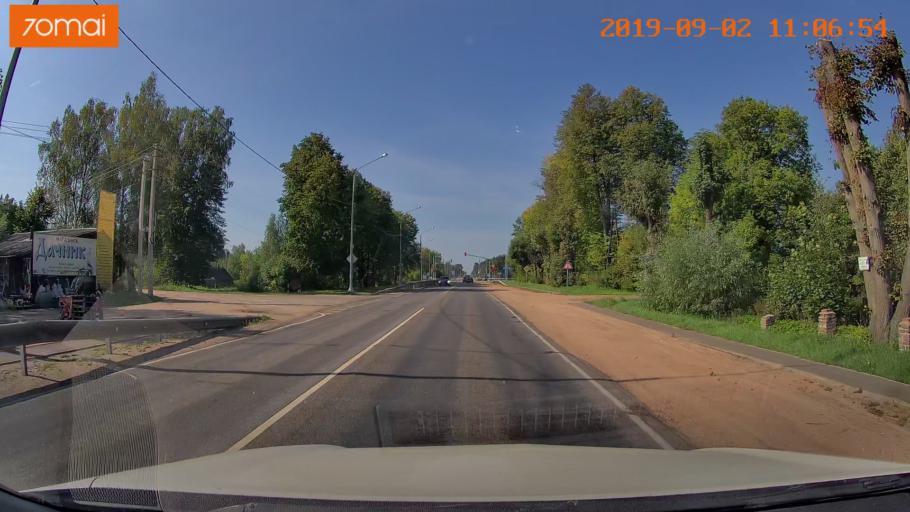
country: RU
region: Smolensk
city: Yekimovichi
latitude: 54.1125
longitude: 33.2871
